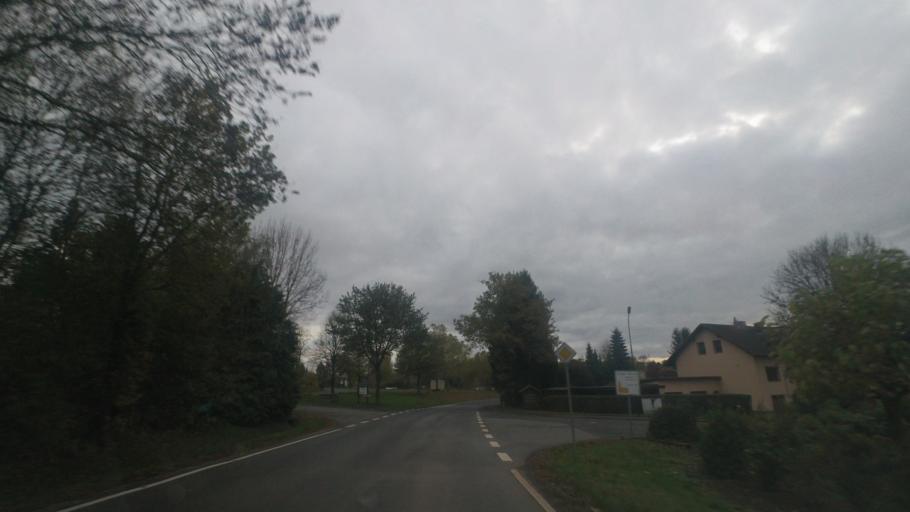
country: DE
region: Hesse
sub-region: Regierungsbezirk Giessen
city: Freiensteinau
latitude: 50.3722
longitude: 9.4247
